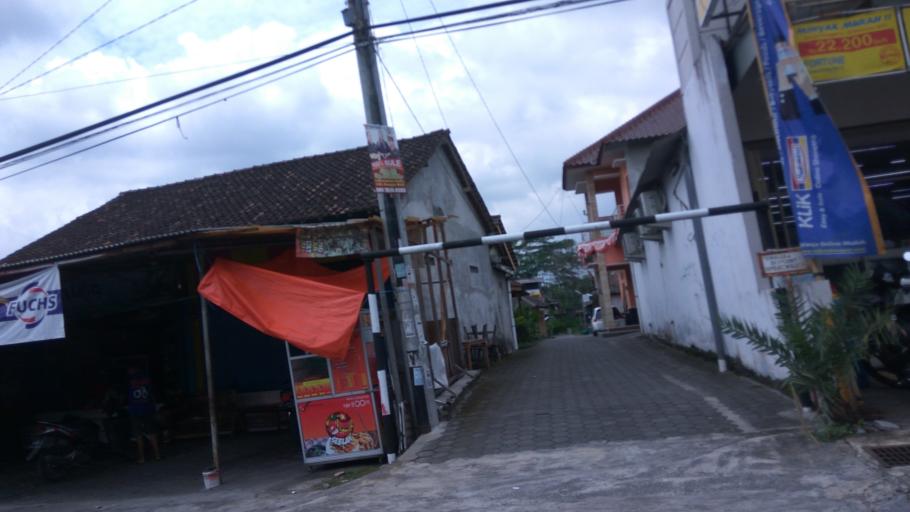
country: ID
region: Daerah Istimewa Yogyakarta
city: Depok
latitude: -7.7472
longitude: 110.4123
